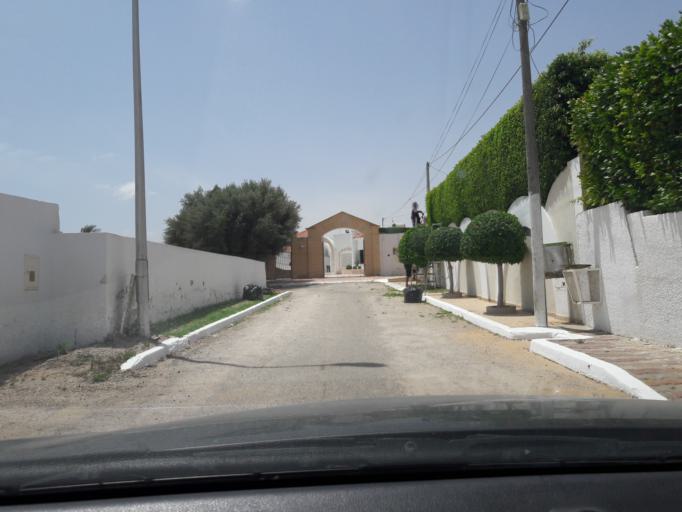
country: TN
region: Safaqis
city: Al Qarmadah
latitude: 34.7802
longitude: 10.7598
